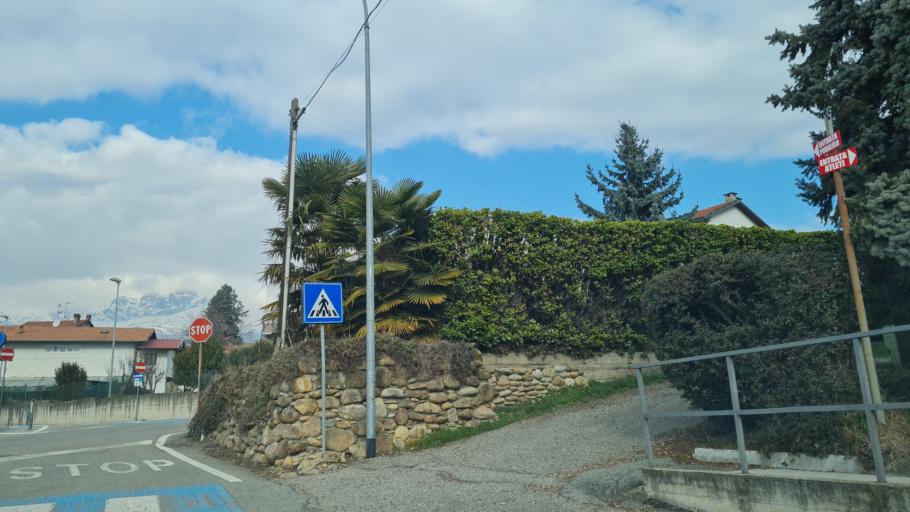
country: IT
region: Piedmont
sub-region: Provincia di Biella
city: Occhieppo Inferiore
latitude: 45.5533
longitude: 8.0252
